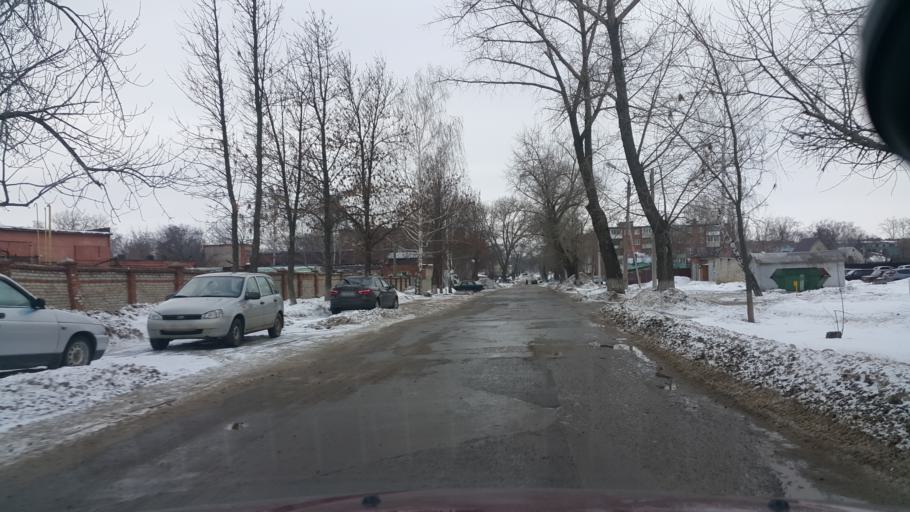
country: RU
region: Tambov
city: Kotovsk
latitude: 52.5958
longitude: 41.5052
